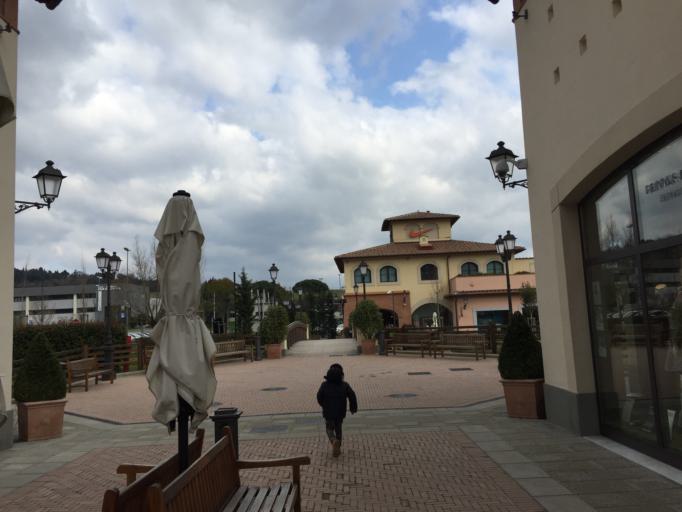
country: IT
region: Tuscany
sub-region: Province of Florence
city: Cavallina
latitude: 43.9858
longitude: 11.2128
